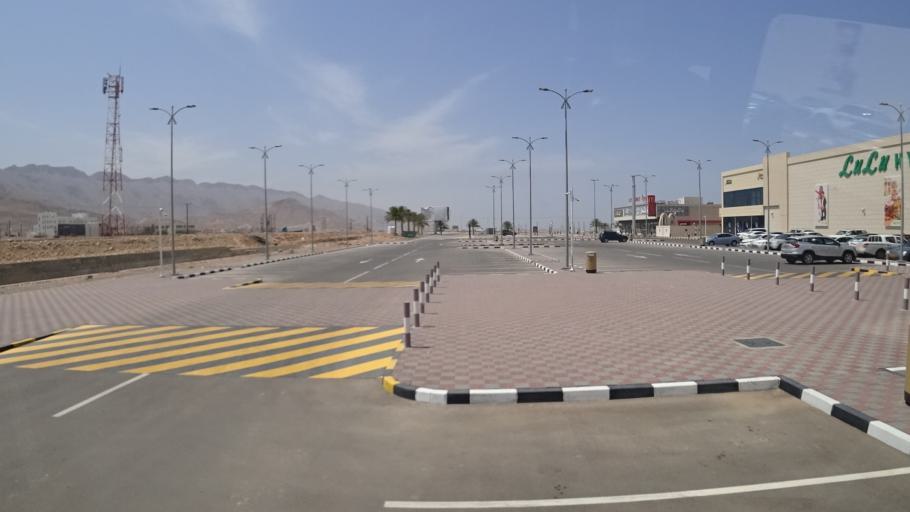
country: OM
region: Ash Sharqiyah
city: Sur
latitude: 22.5950
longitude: 59.4376
